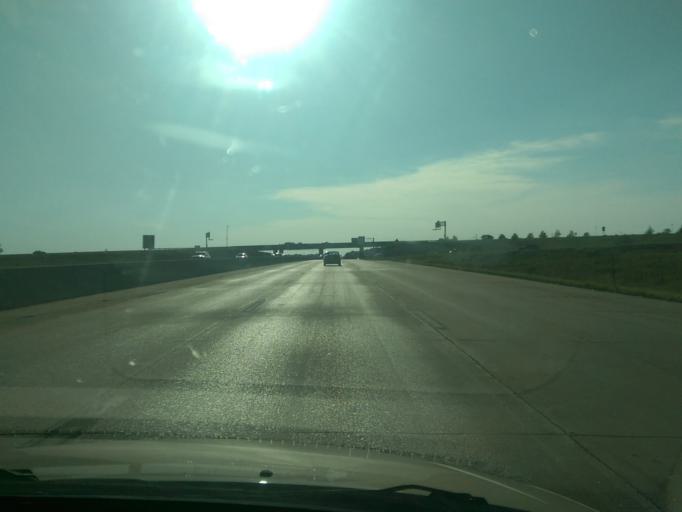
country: US
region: Missouri
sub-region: Jackson County
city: East Independence
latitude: 39.0414
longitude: -94.3590
